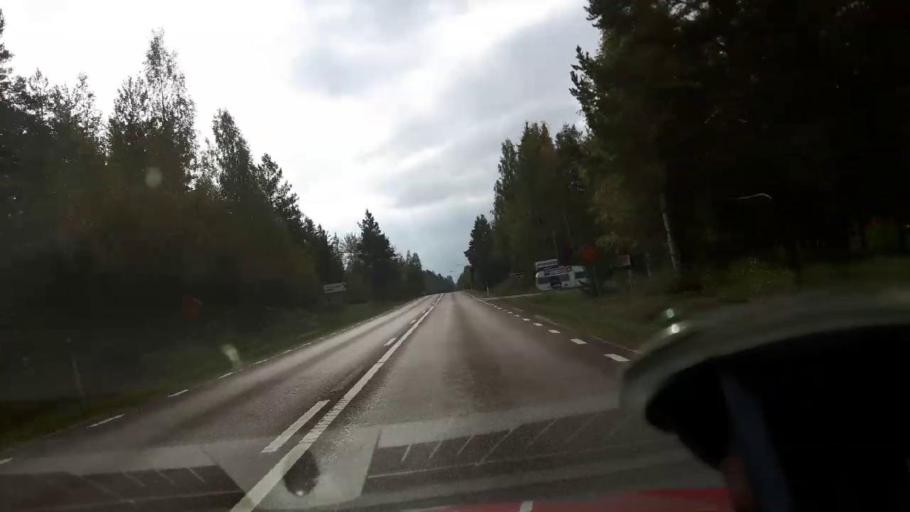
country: SE
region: Gaevleborg
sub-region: Bollnas Kommun
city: Kilafors
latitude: 61.2557
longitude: 16.5522
